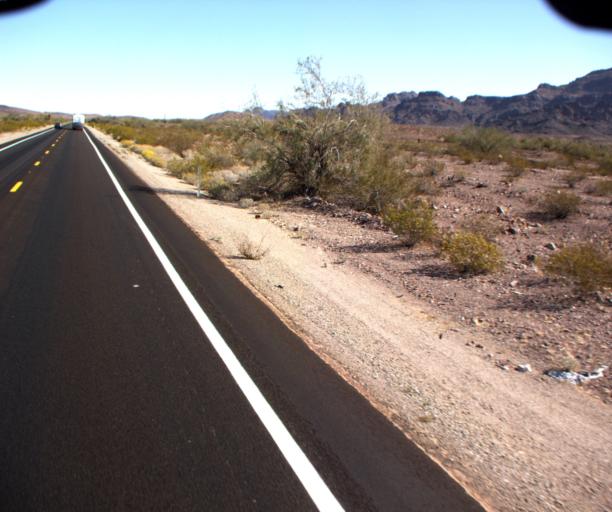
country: US
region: Arizona
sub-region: La Paz County
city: Quartzsite
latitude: 33.2064
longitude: -114.2657
